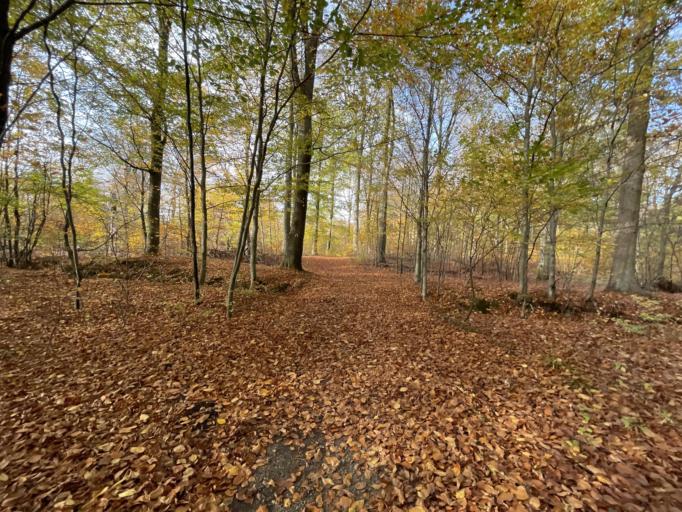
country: DK
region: Capital Region
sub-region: Fureso Kommune
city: Vaerlose
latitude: 55.7635
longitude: 12.4124
